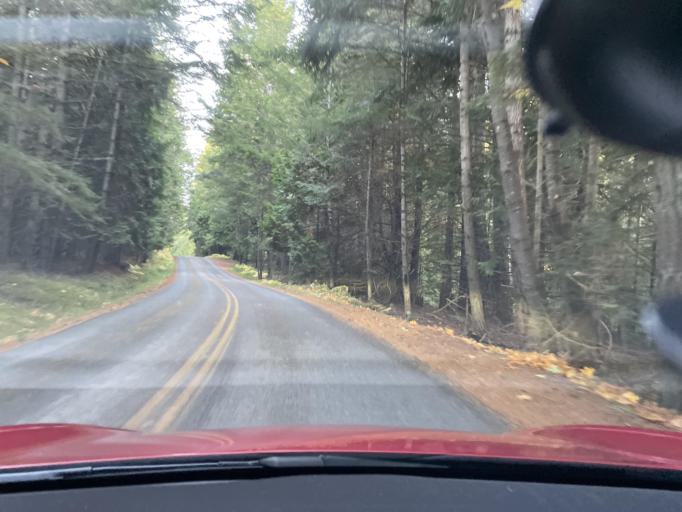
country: US
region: Washington
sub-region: San Juan County
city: Friday Harbor
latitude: 48.5256
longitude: -123.1461
